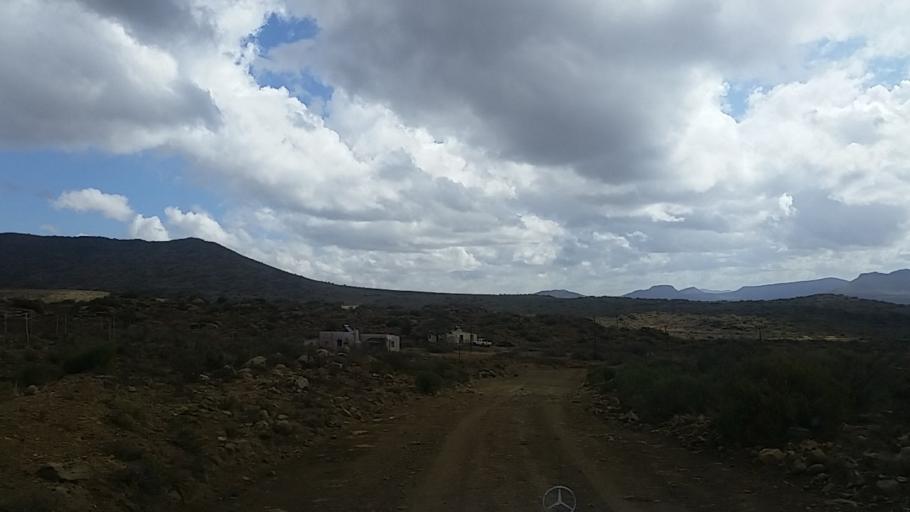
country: ZA
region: Eastern Cape
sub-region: Chris Hani District Municipality
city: Middelburg
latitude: -31.7916
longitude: 24.6619
